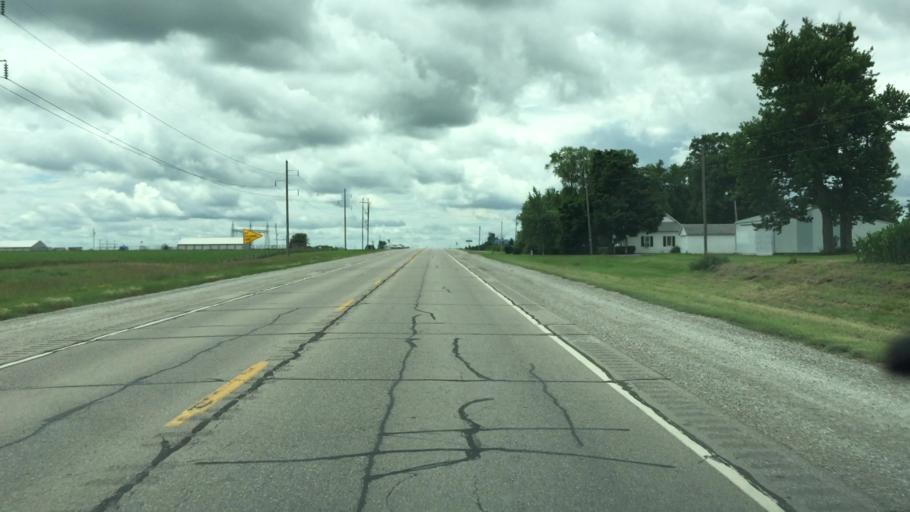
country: US
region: Iowa
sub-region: Jasper County
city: Monroe
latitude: 41.5764
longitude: -93.0971
